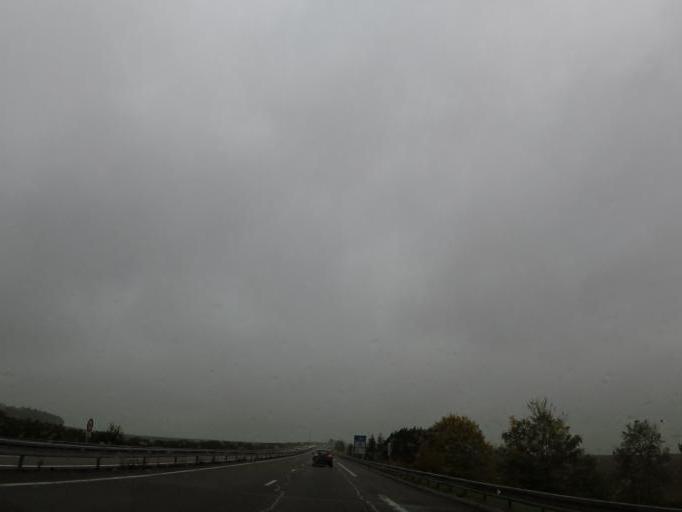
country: FR
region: Champagne-Ardenne
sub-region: Departement de la Marne
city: Courtisols
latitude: 49.0338
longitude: 4.4556
